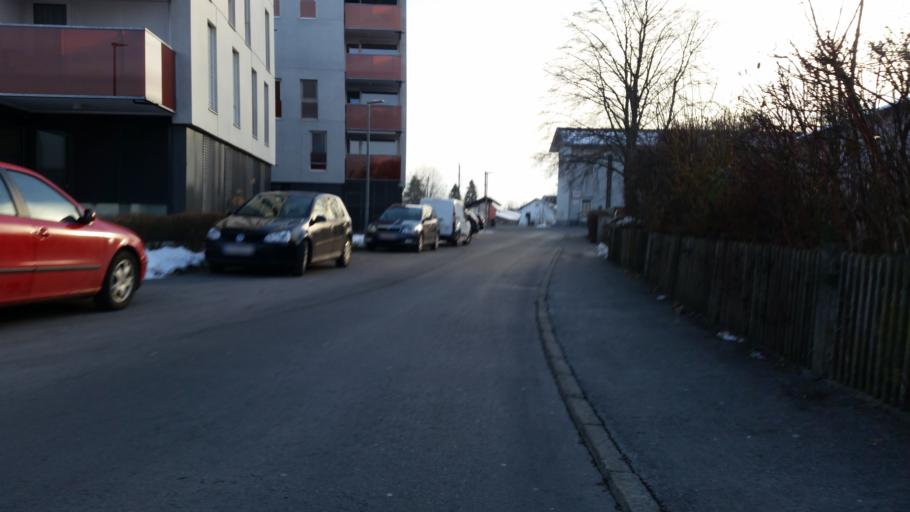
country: AT
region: Vorarlberg
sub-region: Politischer Bezirk Bregenz
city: Hard
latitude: 47.4808
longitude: 9.6884
